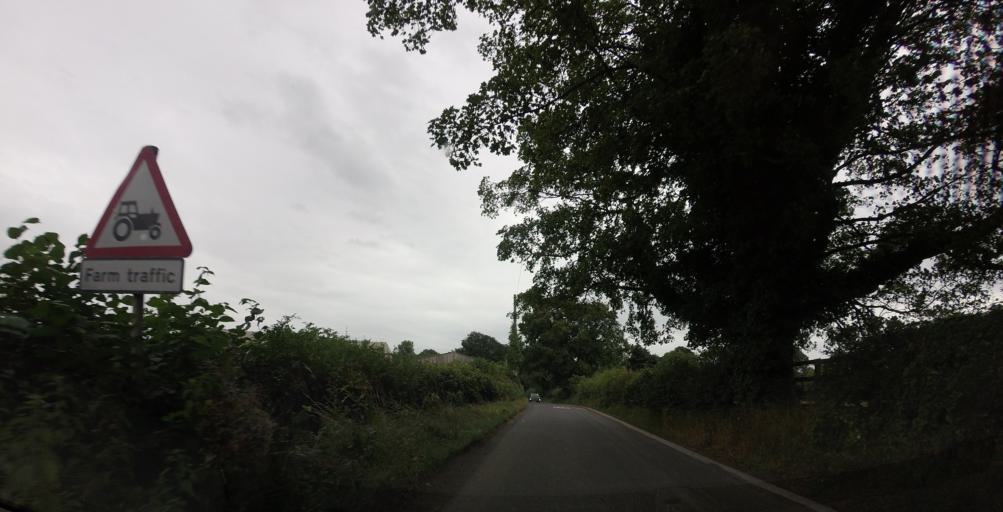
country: GB
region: England
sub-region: North Yorkshire
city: Ripon
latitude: 54.1156
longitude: -1.5183
